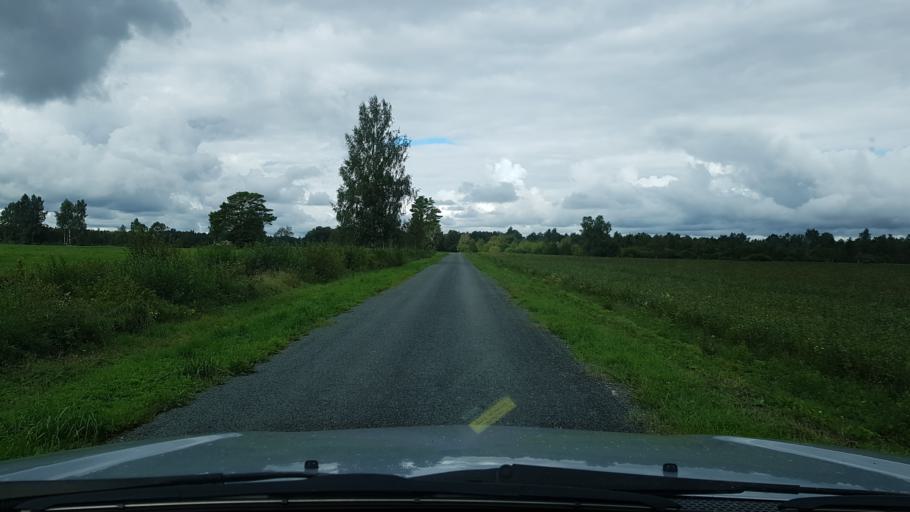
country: EE
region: Harju
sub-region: Raasiku vald
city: Arukula
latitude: 59.2814
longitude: 25.0747
